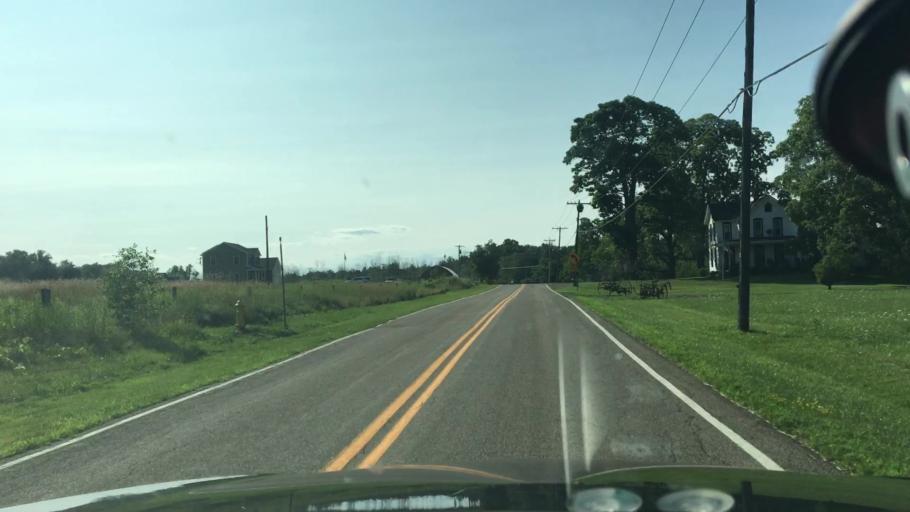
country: US
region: New York
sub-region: Erie County
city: North Collins
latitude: 42.6283
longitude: -78.9779
